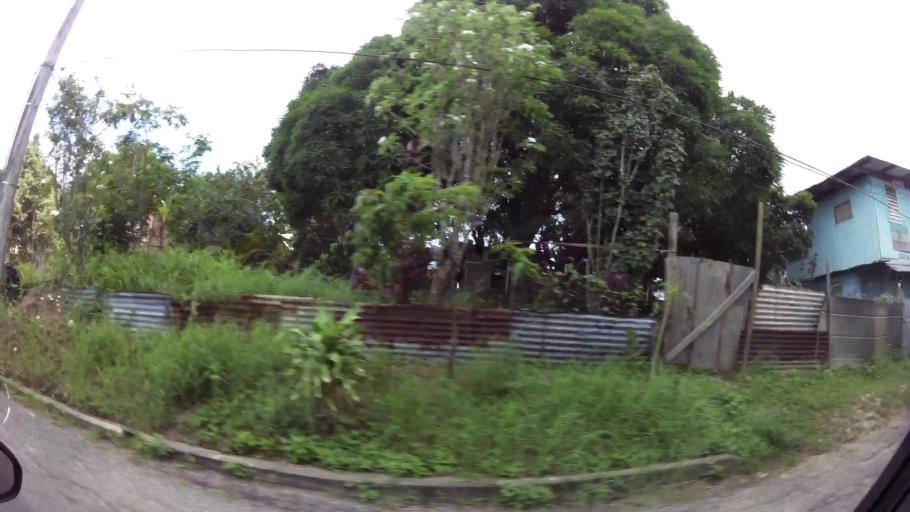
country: TT
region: City of San Fernando
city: Mon Repos
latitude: 10.2696
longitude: -61.4496
